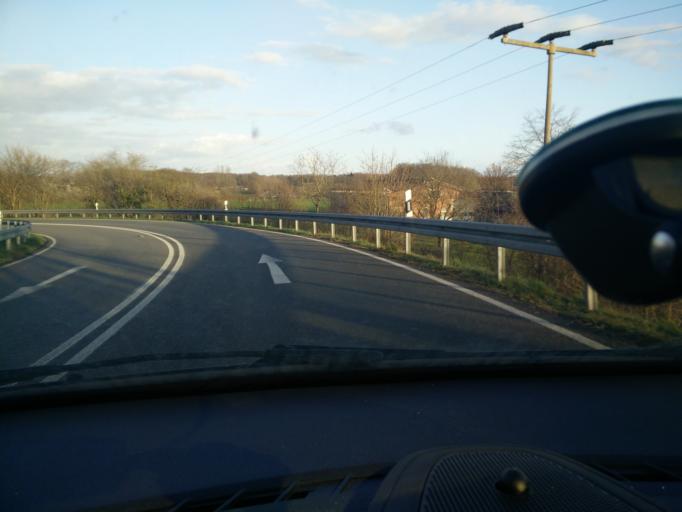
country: DE
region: North Rhine-Westphalia
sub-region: Regierungsbezirk Munster
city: Borken
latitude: 51.8387
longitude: 6.8836
